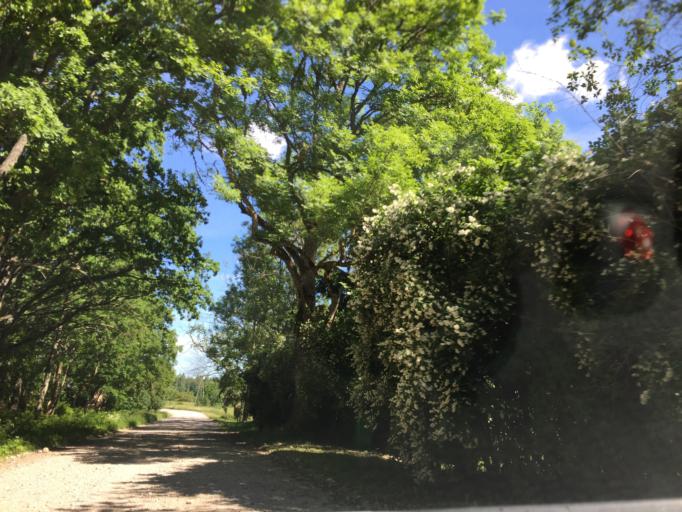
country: LV
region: Dundaga
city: Dundaga
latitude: 57.3589
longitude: 22.0309
